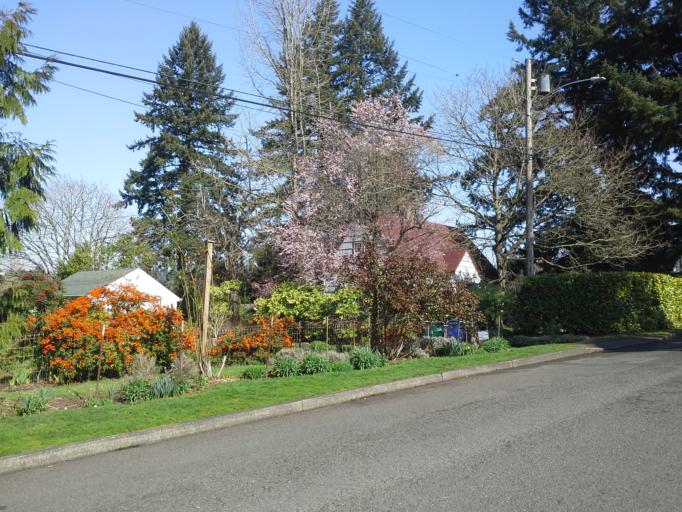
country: US
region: Oregon
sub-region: Washington County
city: Garden Home-Whitford
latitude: 45.4690
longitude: -122.7162
